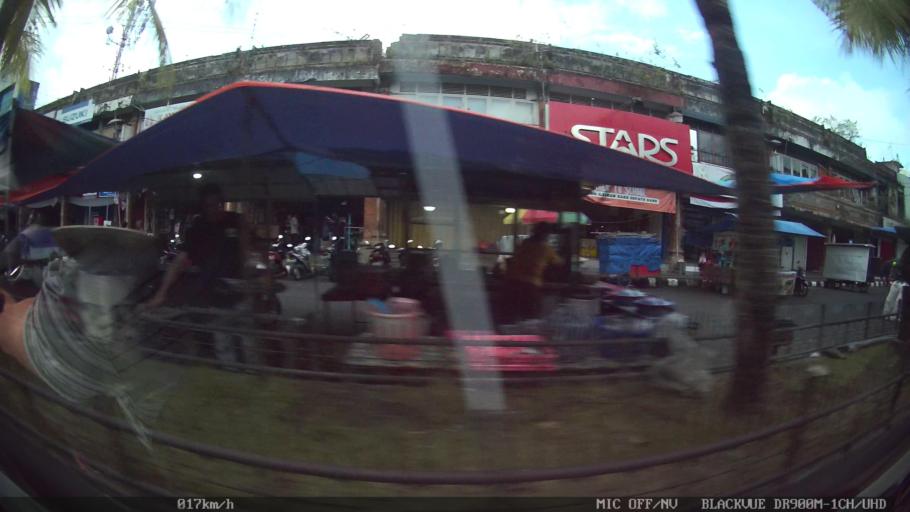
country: ID
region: Bali
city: Tabanan
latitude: -8.5387
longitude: 115.1249
